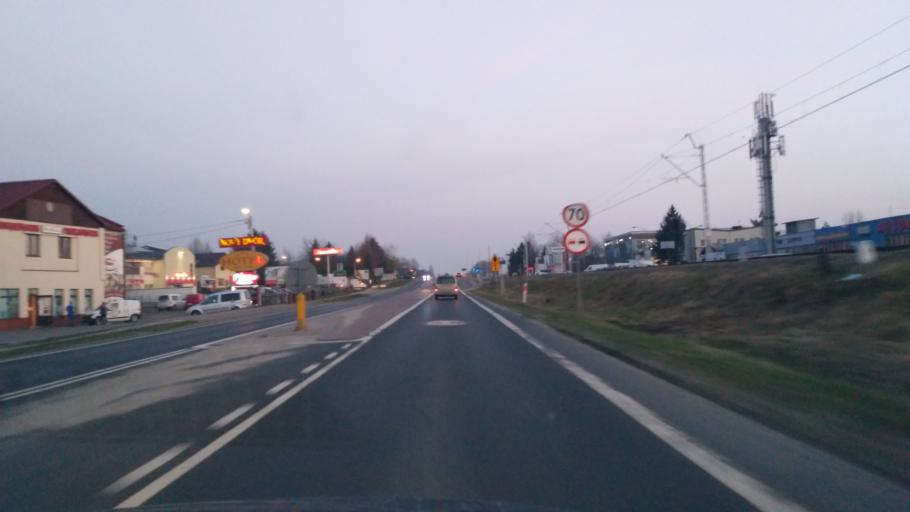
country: PL
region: Subcarpathian Voivodeship
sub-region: Powiat rzeszowski
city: Rudna Mala
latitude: 50.0840
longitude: 21.9843
